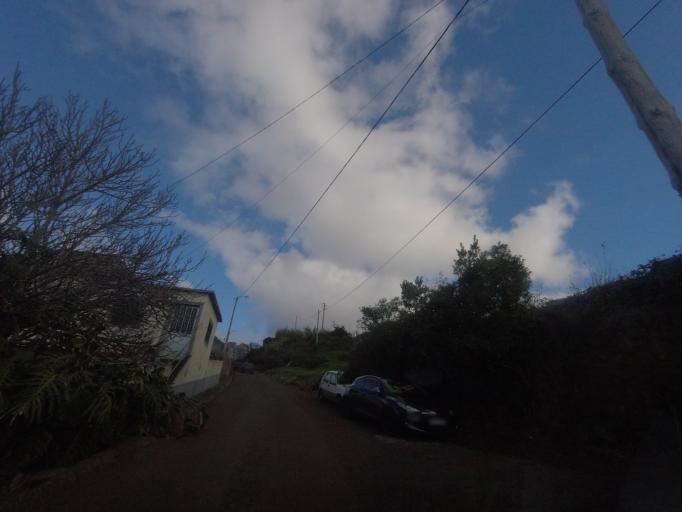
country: PT
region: Madeira
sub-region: Calheta
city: Faja da Ovelha
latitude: 32.8261
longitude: -17.2355
